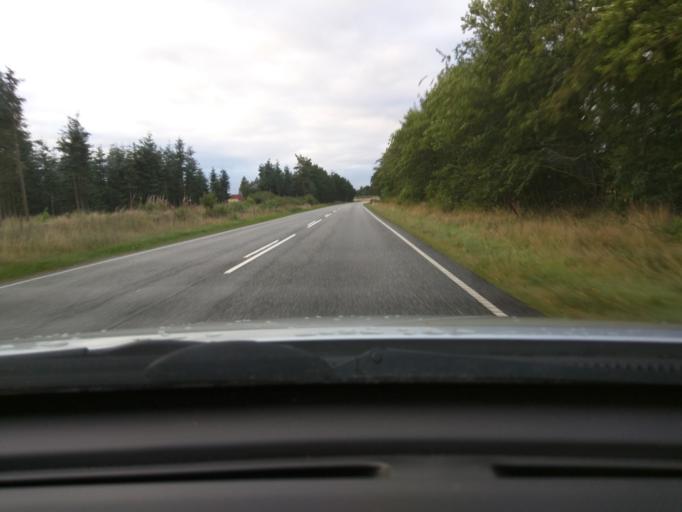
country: DK
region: Central Jutland
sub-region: Ikast-Brande Kommune
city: Bording Kirkeby
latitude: 56.2549
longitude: 9.3188
